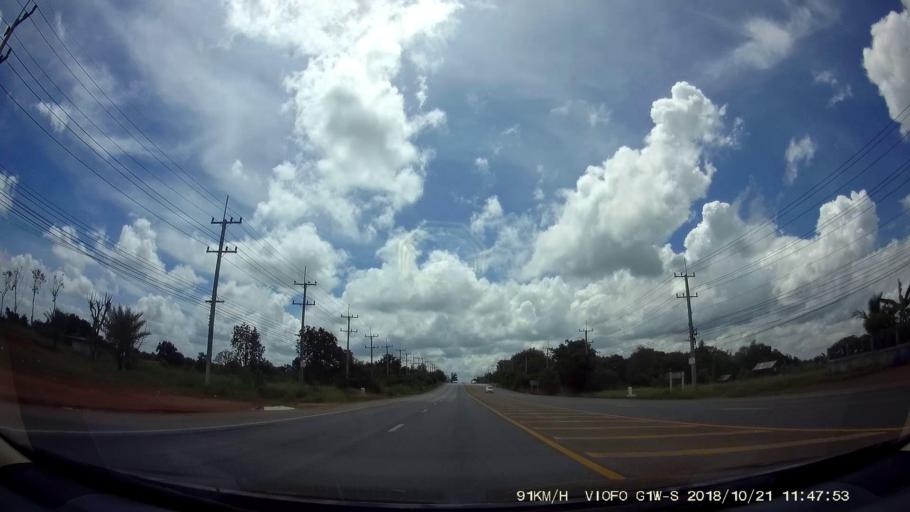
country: TH
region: Chaiyaphum
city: Noen Sa-nga
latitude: 15.6552
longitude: 101.9517
